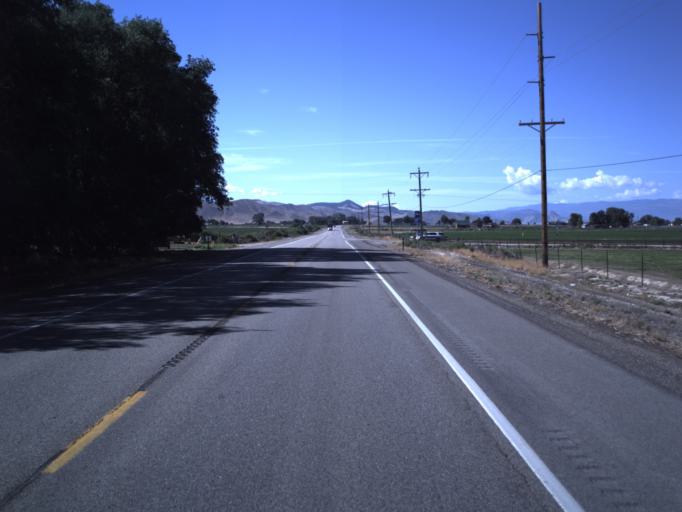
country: US
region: Utah
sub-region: Sanpete County
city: Centerfield
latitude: 39.0710
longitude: -111.8209
